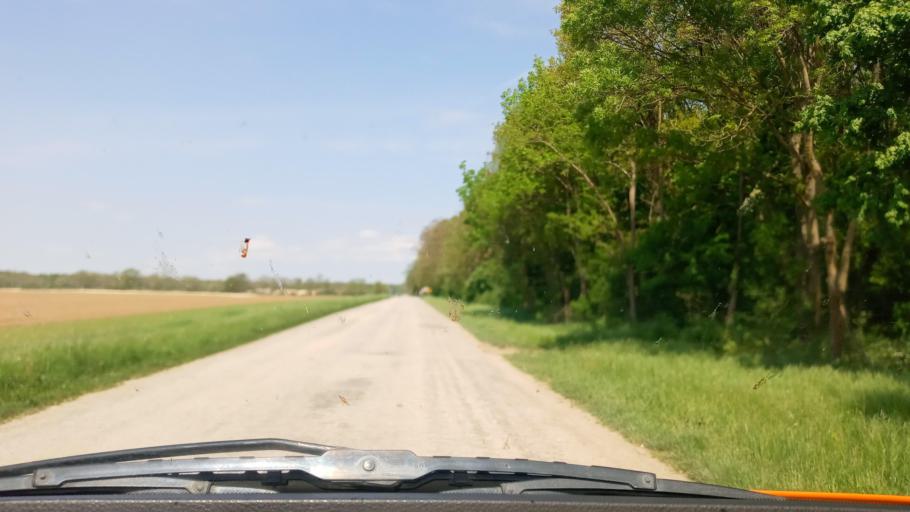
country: HU
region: Baranya
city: Boly
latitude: 45.8838
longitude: 18.5694
